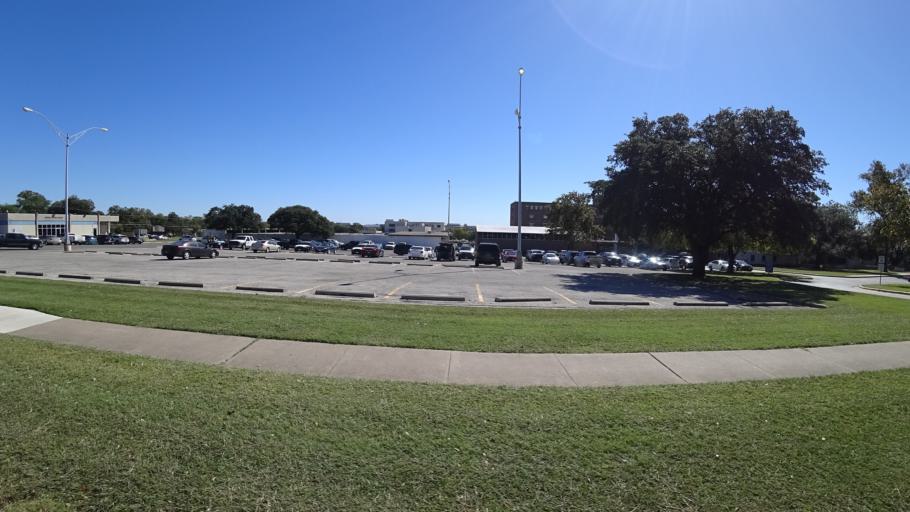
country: US
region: Texas
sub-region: Travis County
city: Austin
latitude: 30.3292
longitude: -97.7242
